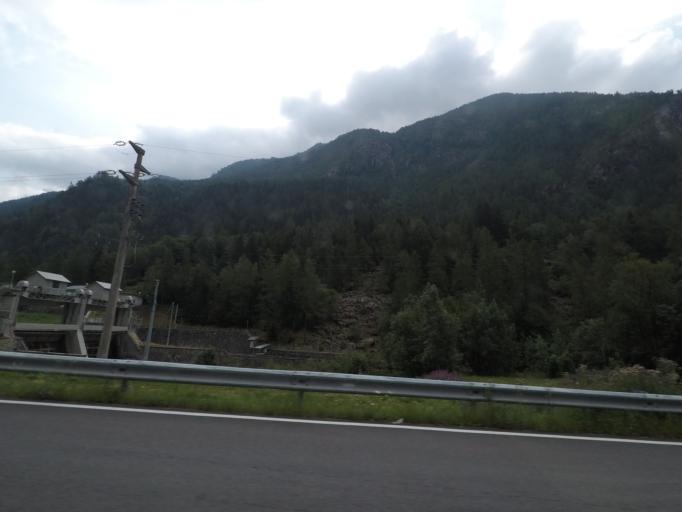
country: IT
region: Aosta Valley
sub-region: Valle d'Aosta
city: Chamois
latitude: 45.8574
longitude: 7.6083
